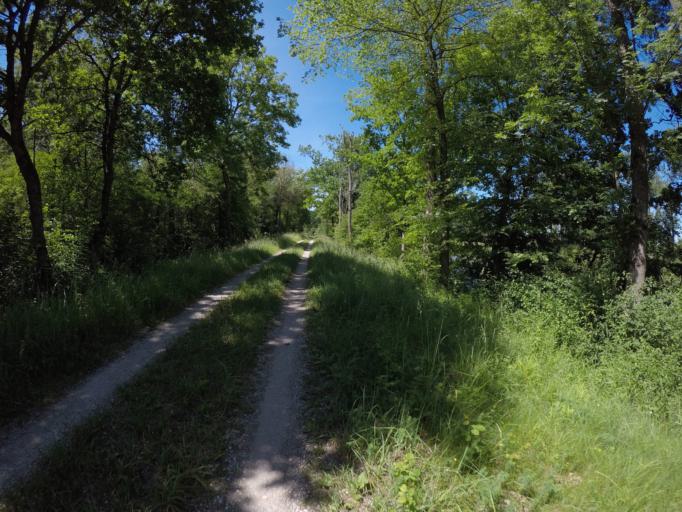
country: DE
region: Bavaria
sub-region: Upper Bavaria
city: Langenbach
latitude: 48.4620
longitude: 11.8812
